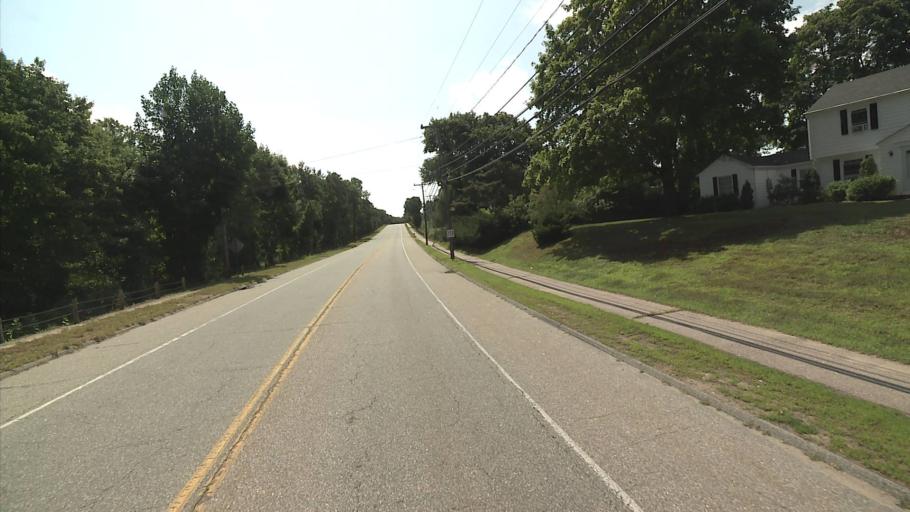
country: US
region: Connecticut
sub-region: New London County
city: Central Waterford
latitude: 41.3397
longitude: -72.1378
